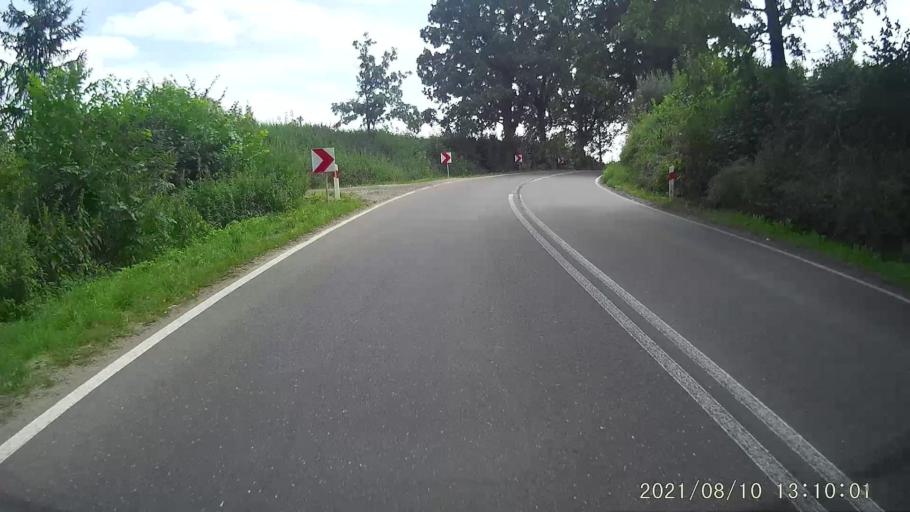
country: PL
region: Lower Silesian Voivodeship
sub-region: Powiat klodzki
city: Bozkow
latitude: 50.5005
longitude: 16.5352
